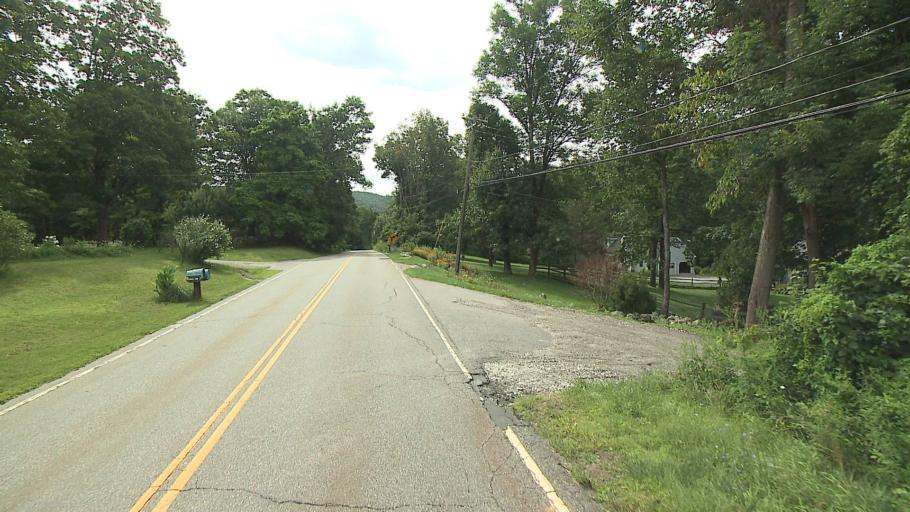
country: US
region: Connecticut
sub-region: Litchfield County
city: Kent
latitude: 41.7438
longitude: -73.5010
